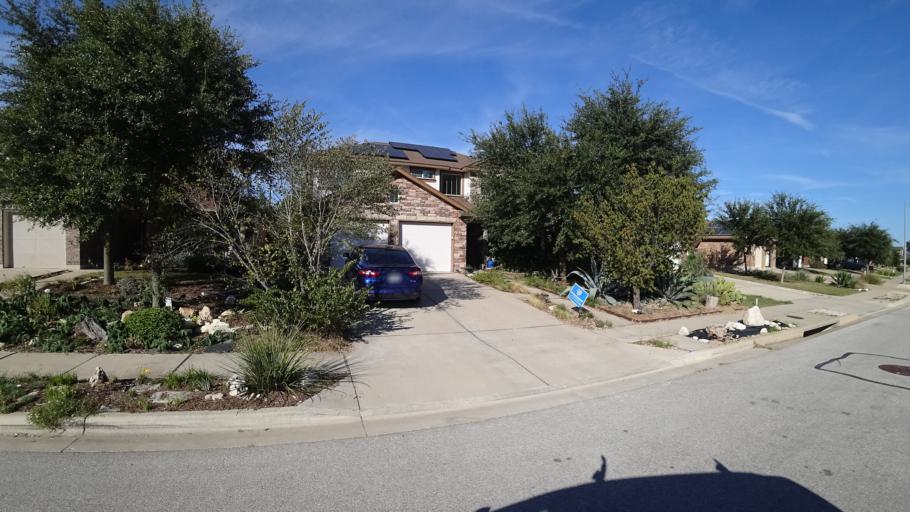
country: US
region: Texas
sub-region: Travis County
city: Austin
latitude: 30.2613
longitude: -97.6692
